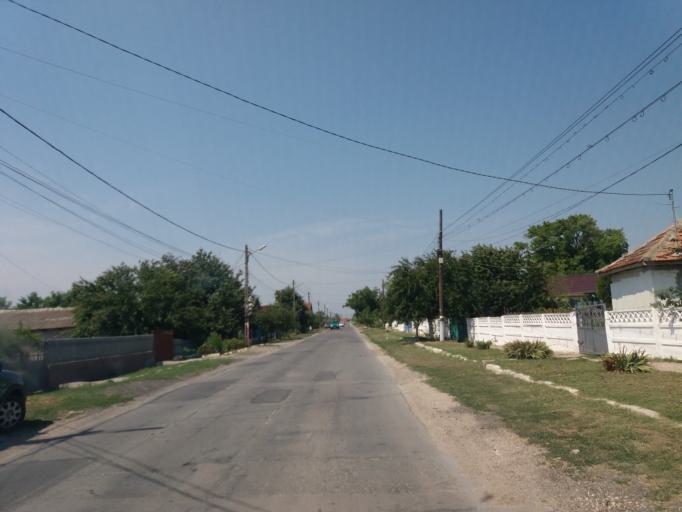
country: RO
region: Constanta
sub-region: Comuna Corbu
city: Corbu
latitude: 44.3997
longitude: 28.6617
